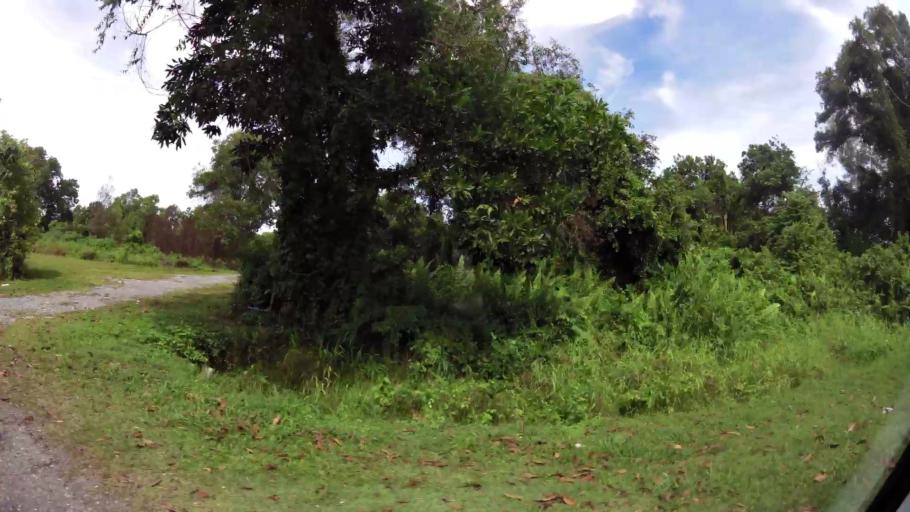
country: BN
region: Belait
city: Seria
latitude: 4.6019
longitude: 114.3100
